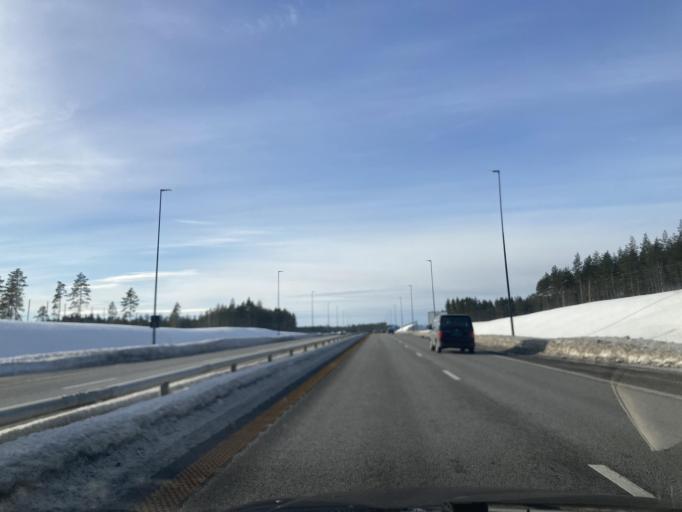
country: NO
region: Hedmark
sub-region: Loten
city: Loten
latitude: 60.8568
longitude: 11.4009
